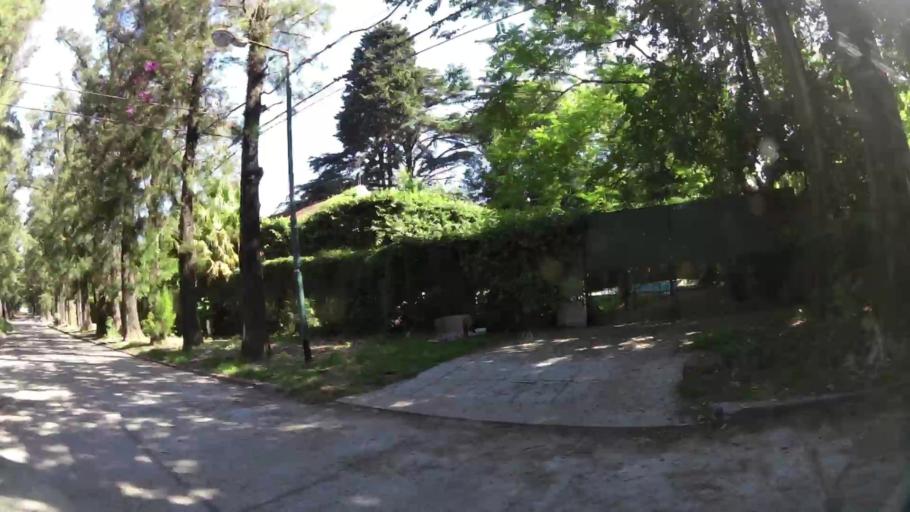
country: AR
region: Buenos Aires
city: Caseros
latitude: -34.5471
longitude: -58.5853
